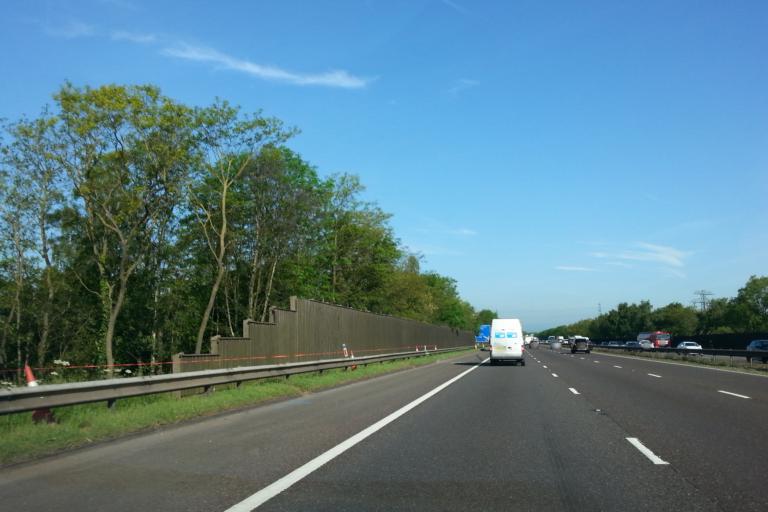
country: GB
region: England
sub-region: Warwickshire
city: Exhall
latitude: 52.4494
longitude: -1.4638
